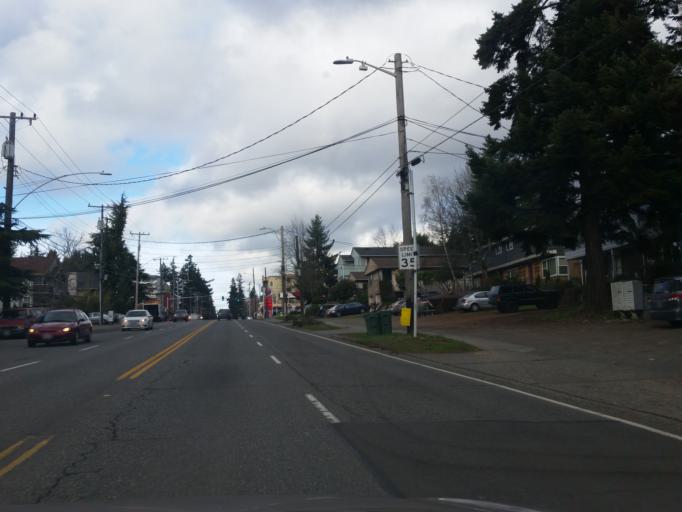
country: US
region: Washington
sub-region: King County
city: Shoreline
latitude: 47.7306
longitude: -122.3556
